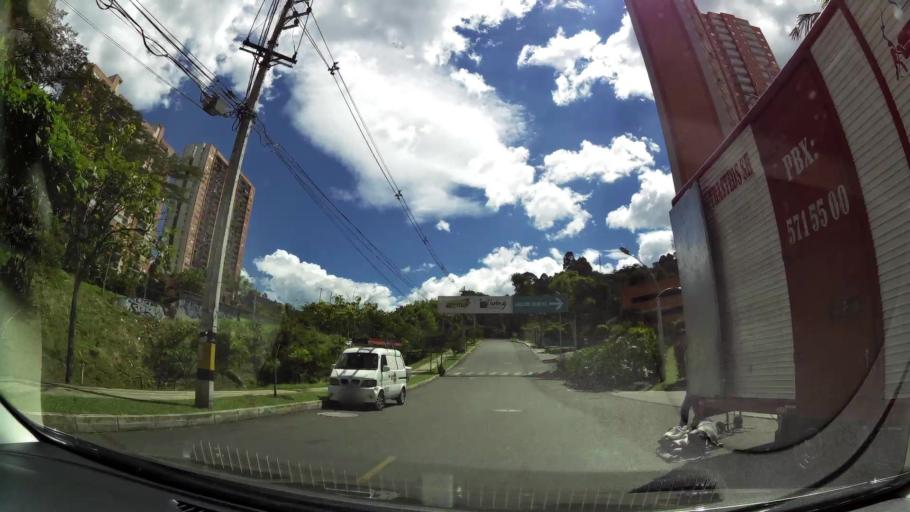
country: CO
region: Antioquia
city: Sabaneta
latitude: 6.1442
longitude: -75.6222
